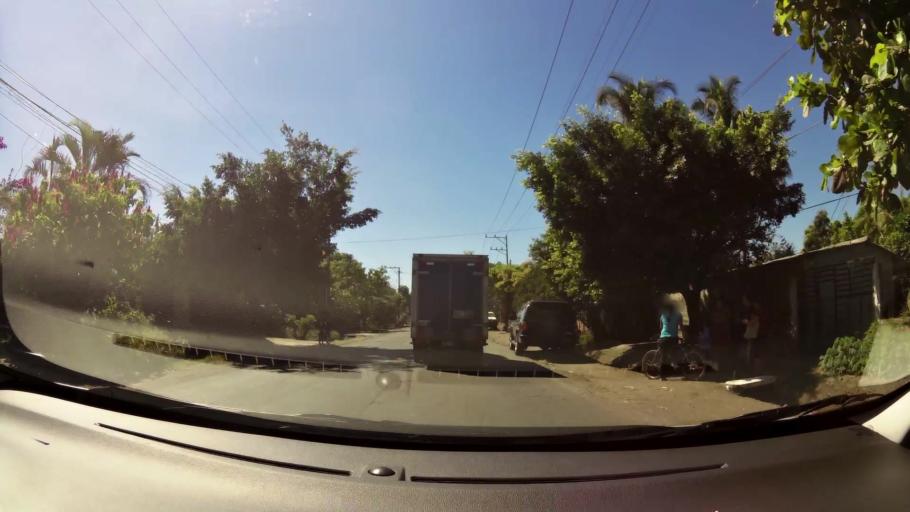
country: SV
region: La Libertad
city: San Juan Opico
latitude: 13.7881
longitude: -89.3701
